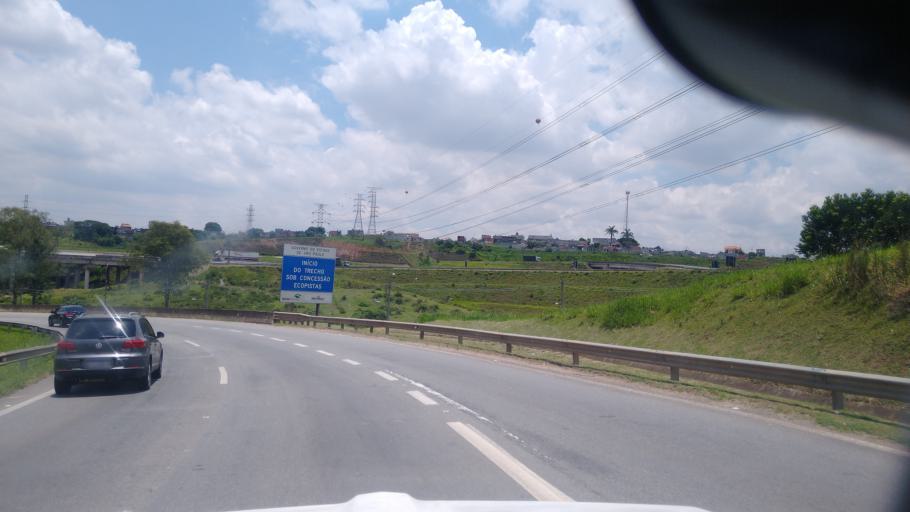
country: BR
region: Sao Paulo
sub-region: Itaquaquecetuba
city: Itaquaquecetuba
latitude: -23.4593
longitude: -46.3449
